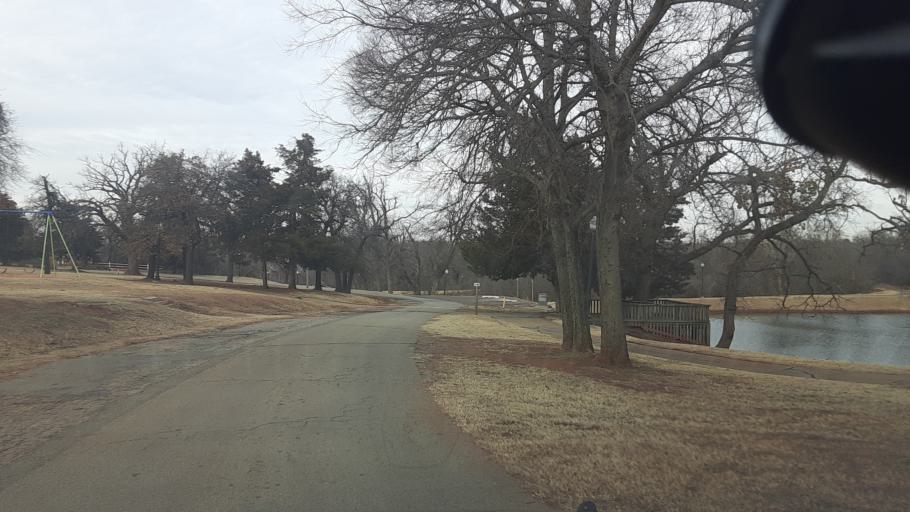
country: US
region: Oklahoma
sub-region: Logan County
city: Guthrie
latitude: 35.8825
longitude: -97.4114
